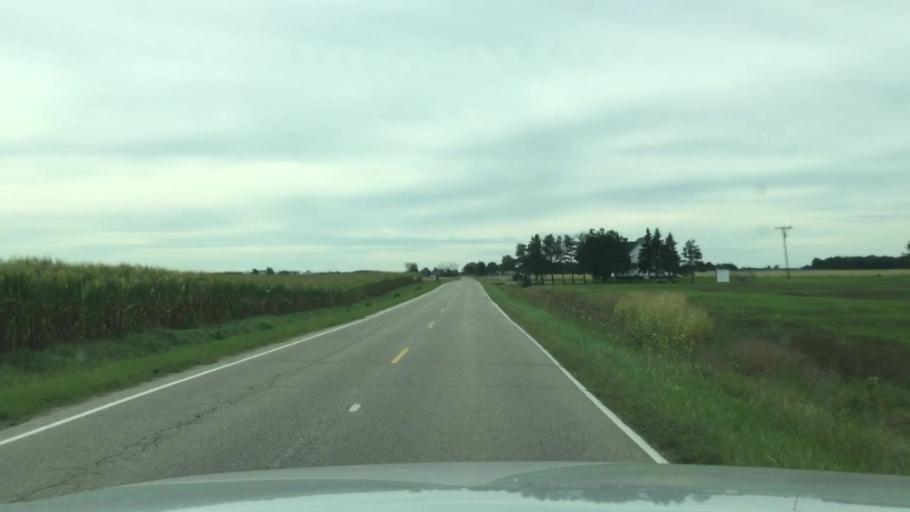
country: US
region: Michigan
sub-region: Genesee County
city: Montrose
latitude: 43.0967
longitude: -83.9878
